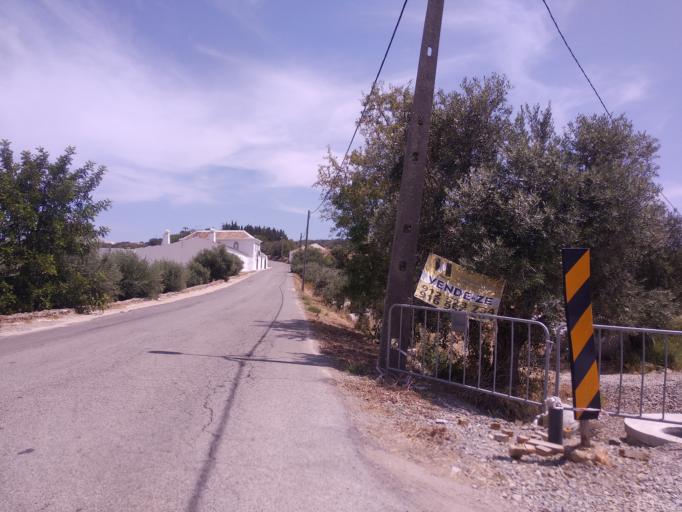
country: PT
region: Faro
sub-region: Sao Bras de Alportel
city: Sao Bras de Alportel
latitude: 37.1473
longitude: -7.9322
